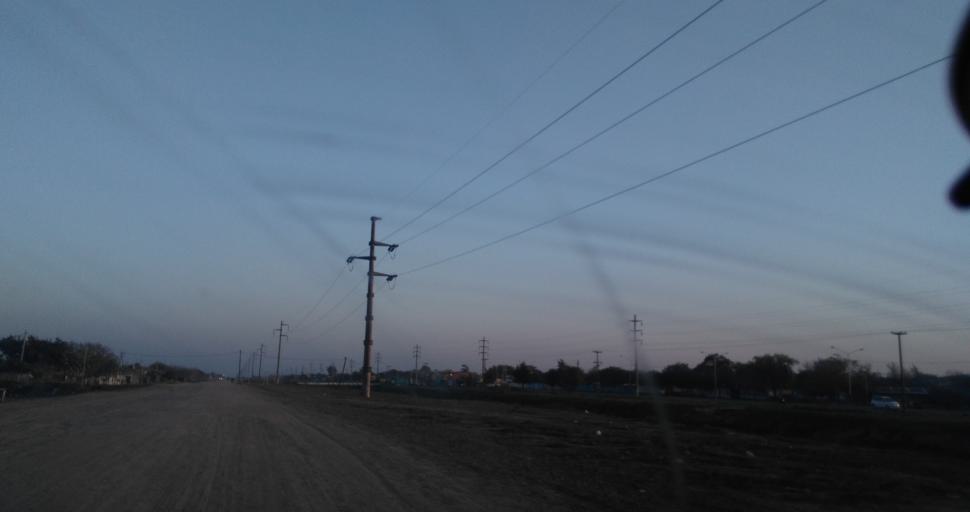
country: AR
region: Chaco
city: Resistencia
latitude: -27.4860
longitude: -58.9917
